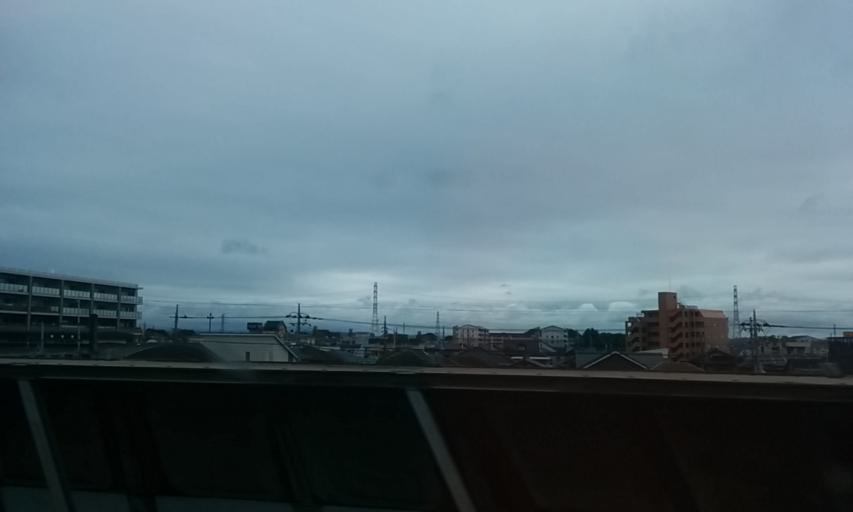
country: JP
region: Tochigi
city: Mibu
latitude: 36.3942
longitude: 139.8536
